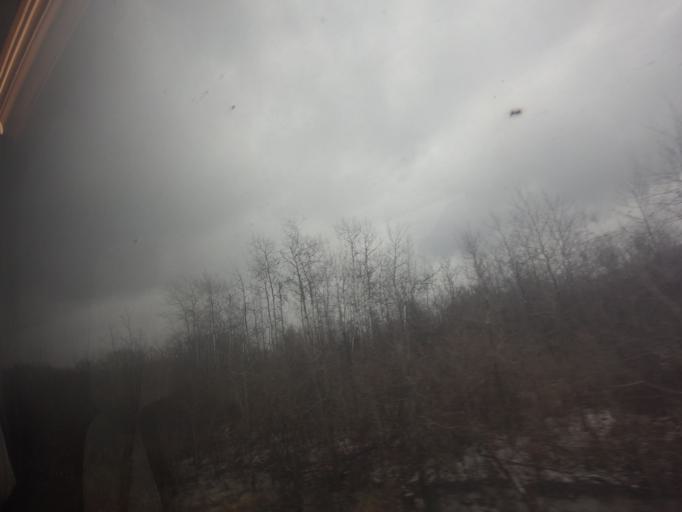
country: CA
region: Ontario
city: Cobourg
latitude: 43.9537
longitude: -78.2642
